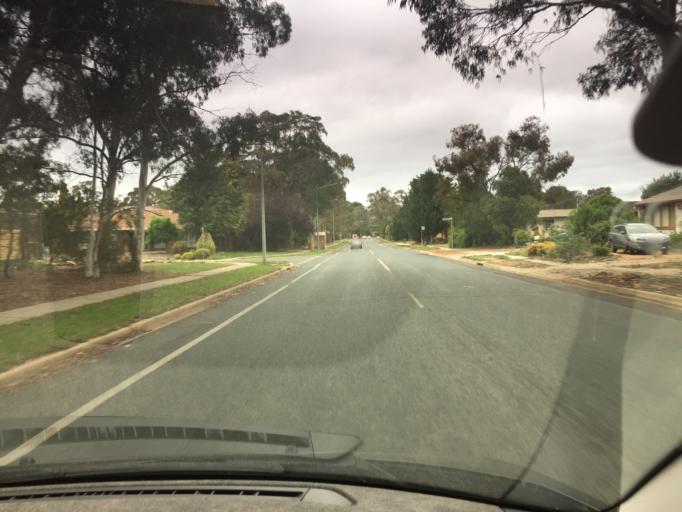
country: AU
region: Australian Capital Territory
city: Kaleen
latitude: -35.2261
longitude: 149.1111
